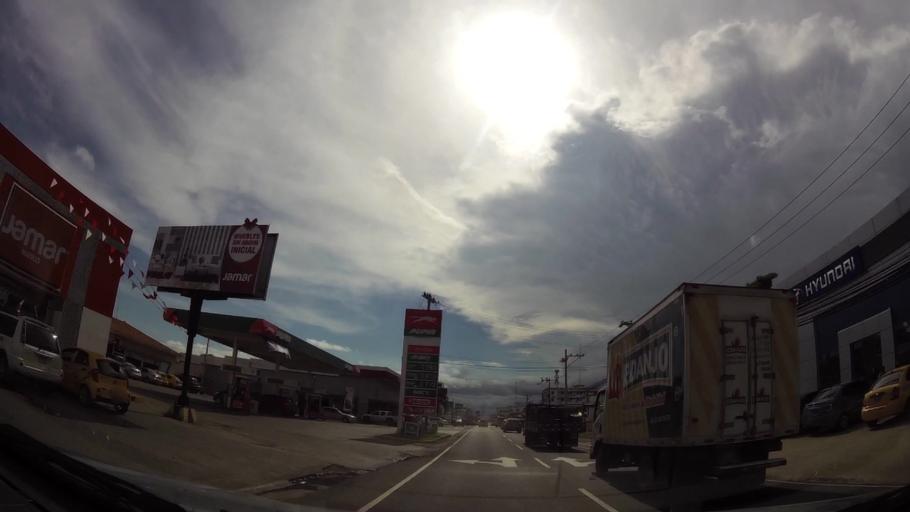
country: PA
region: Panama
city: La Chorrera
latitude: 8.8866
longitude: -79.7740
